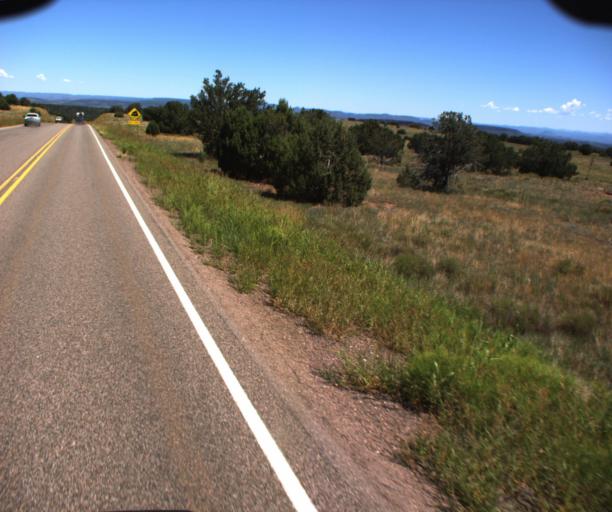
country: US
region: Arizona
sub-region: Navajo County
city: Cibecue
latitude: 33.7185
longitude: -110.5330
